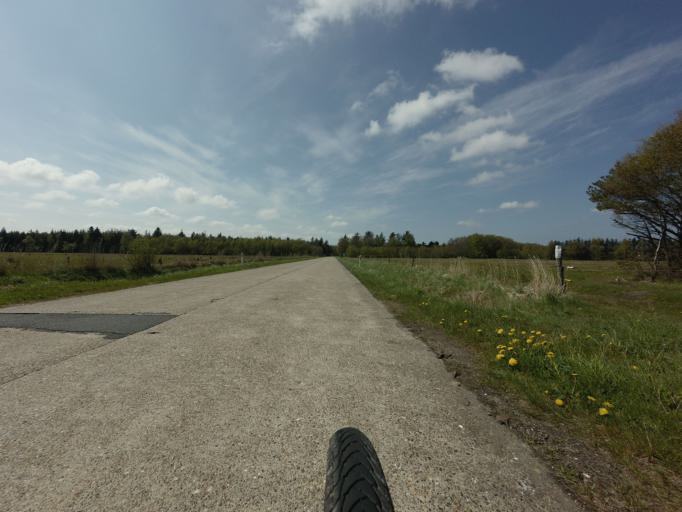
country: DK
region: North Denmark
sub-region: Jammerbugt Kommune
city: Brovst
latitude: 57.1645
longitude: 9.4897
